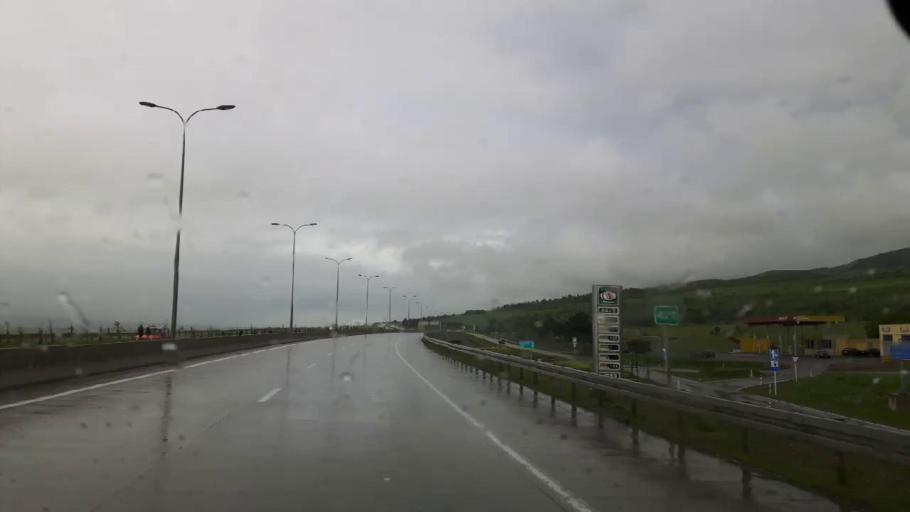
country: GE
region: Shida Kartli
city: Gori
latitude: 42.0258
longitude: 44.2066
